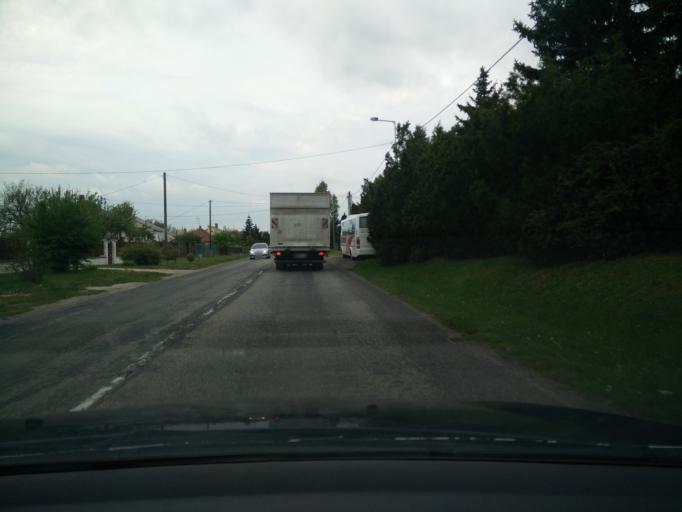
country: HU
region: Gyor-Moson-Sopron
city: Gyorszemere
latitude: 47.5474
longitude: 17.5557
